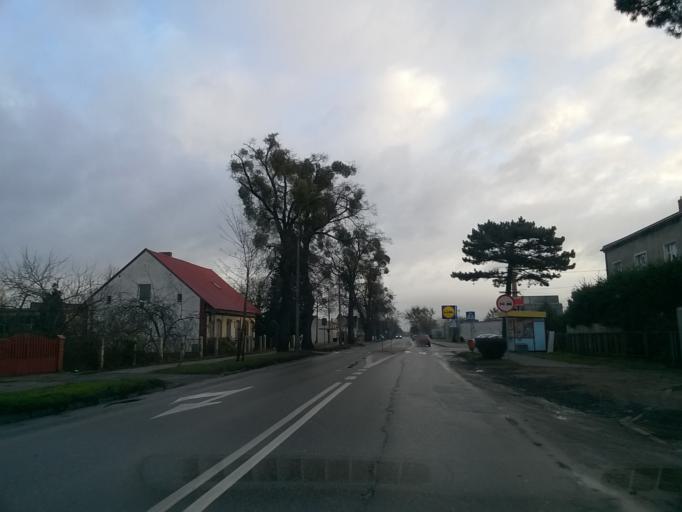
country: PL
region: Greater Poland Voivodeship
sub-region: Powiat wagrowiecki
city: Wagrowiec
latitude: 52.8122
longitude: 17.2121
